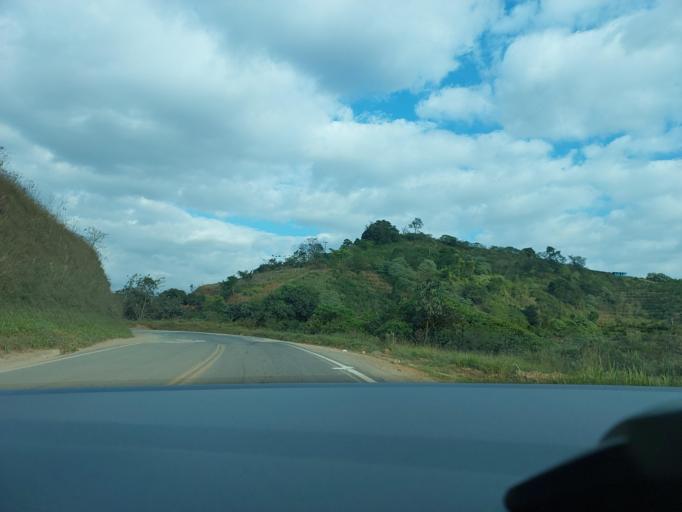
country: BR
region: Minas Gerais
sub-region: Visconde Do Rio Branco
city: Visconde do Rio Branco
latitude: -20.9006
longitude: -42.6538
